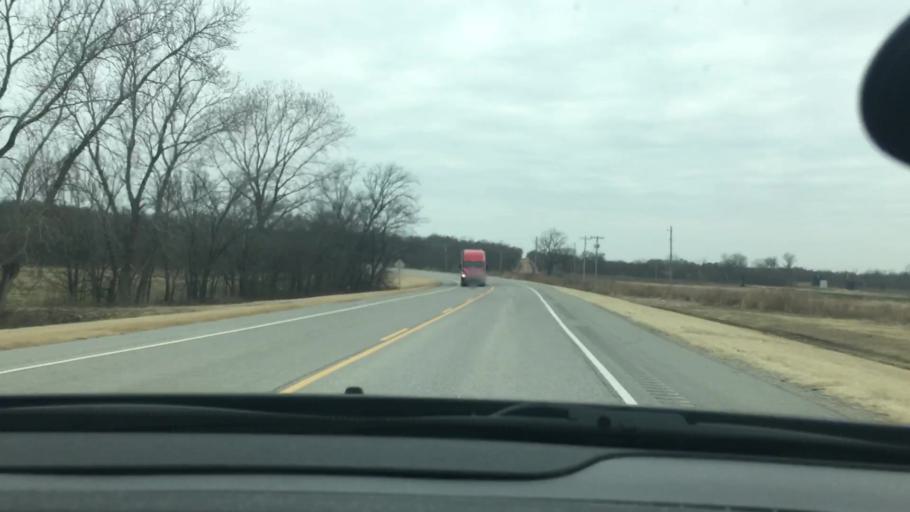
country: US
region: Oklahoma
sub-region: Carter County
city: Healdton
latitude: 34.4925
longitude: -97.4416
